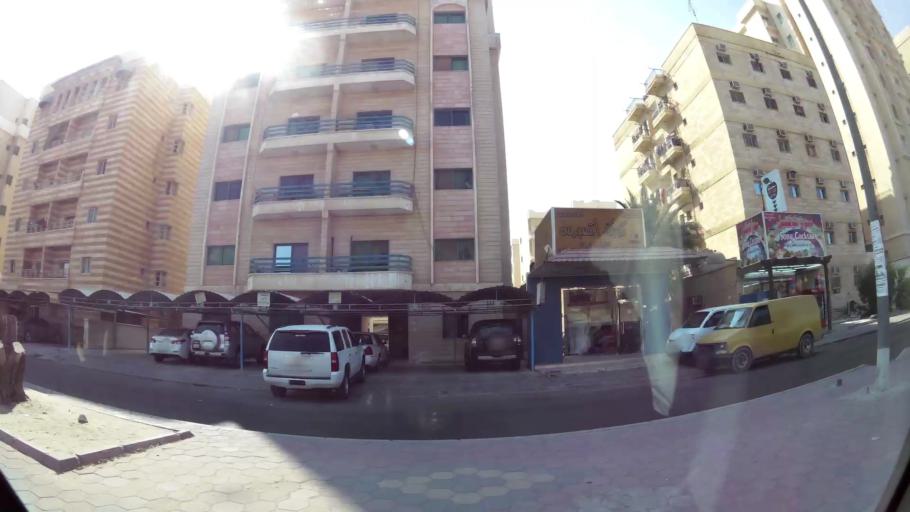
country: KW
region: Al Ahmadi
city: Al Mahbulah
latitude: 29.1330
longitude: 48.1231
